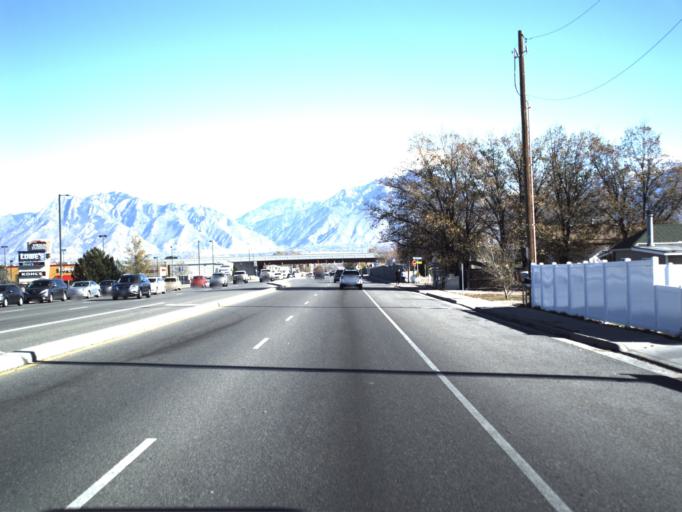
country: US
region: Utah
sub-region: Salt Lake County
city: West Jordan
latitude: 40.6094
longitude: -111.9811
